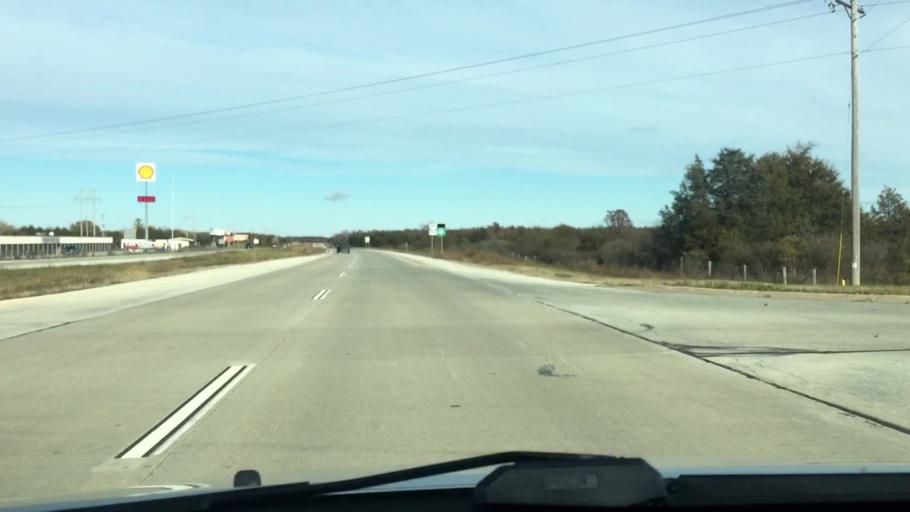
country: US
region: Wisconsin
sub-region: Kewaunee County
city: Luxemburg
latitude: 44.6197
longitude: -87.8249
